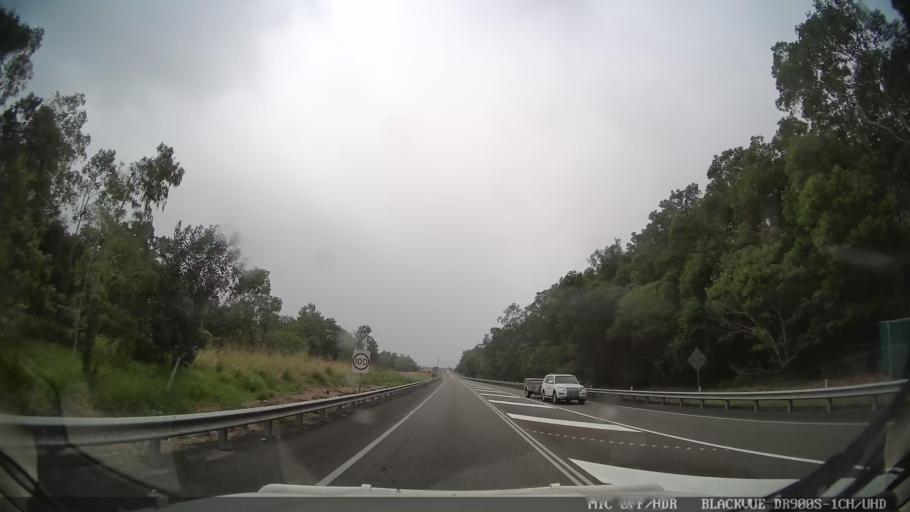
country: AU
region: Queensland
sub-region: Hinchinbrook
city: Ingham
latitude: -18.5141
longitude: 146.1879
